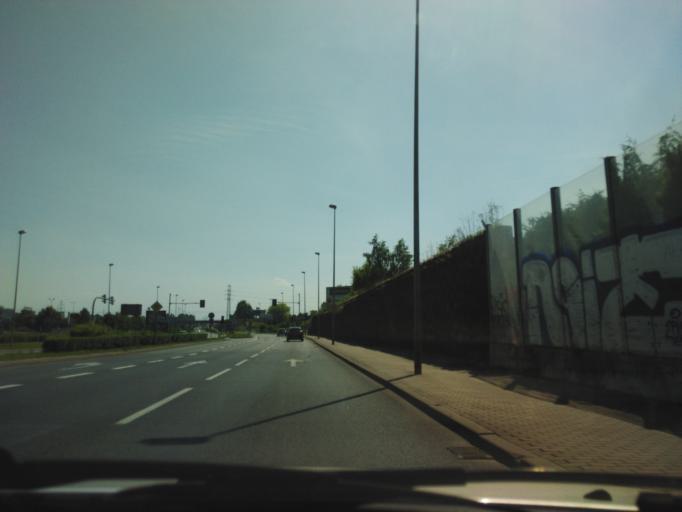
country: PL
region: West Pomeranian Voivodeship
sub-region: Powiat policki
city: Przeclaw
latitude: 53.4017
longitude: 14.5010
